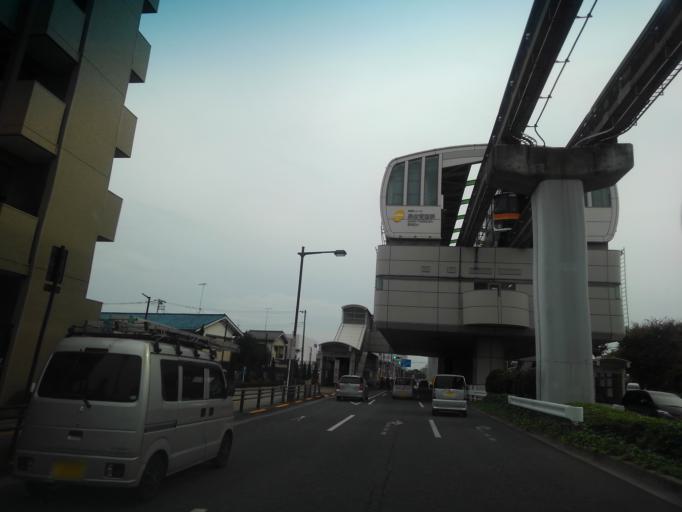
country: JP
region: Tokyo
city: Hino
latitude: 35.7194
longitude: 139.4193
